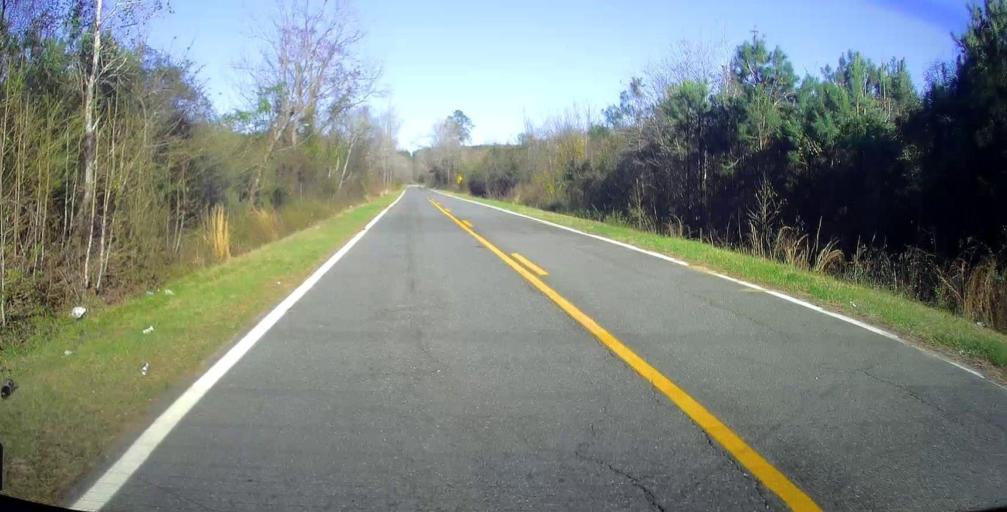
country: US
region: Georgia
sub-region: Taylor County
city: Reynolds
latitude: 32.5472
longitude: -84.0009
